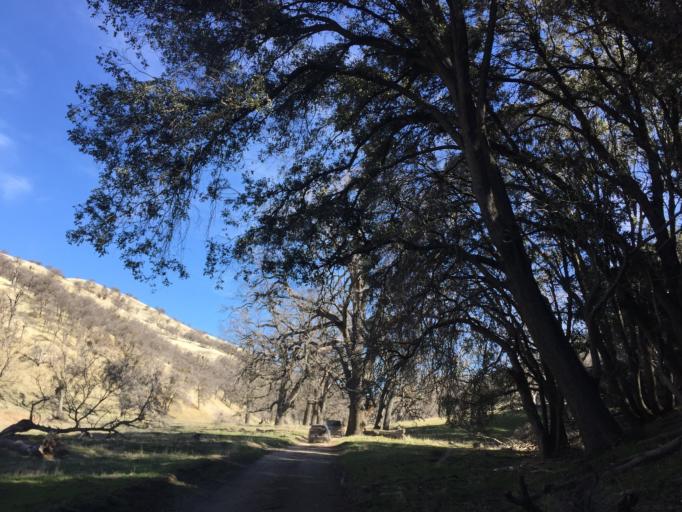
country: US
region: California
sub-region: Kern County
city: Lebec
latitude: 34.8888
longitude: -118.7532
